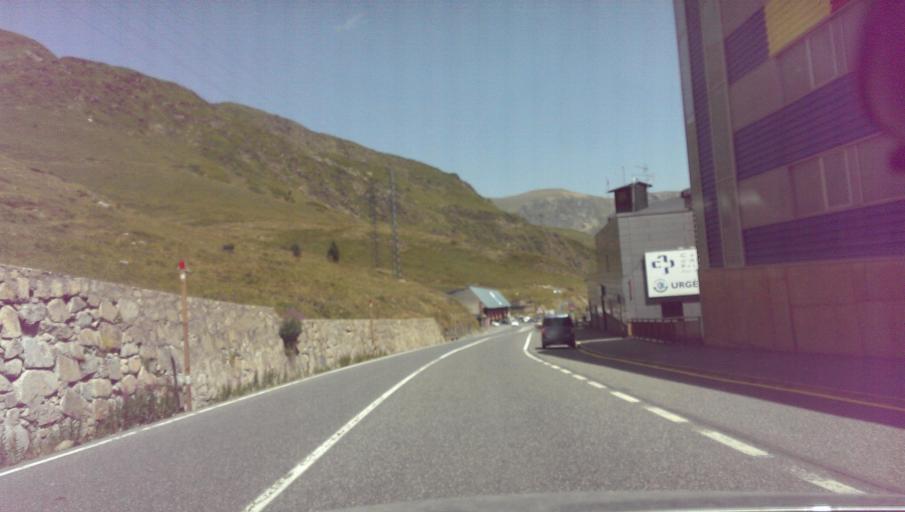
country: AD
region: Encamp
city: Pas de la Casa
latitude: 42.5448
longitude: 1.7307
